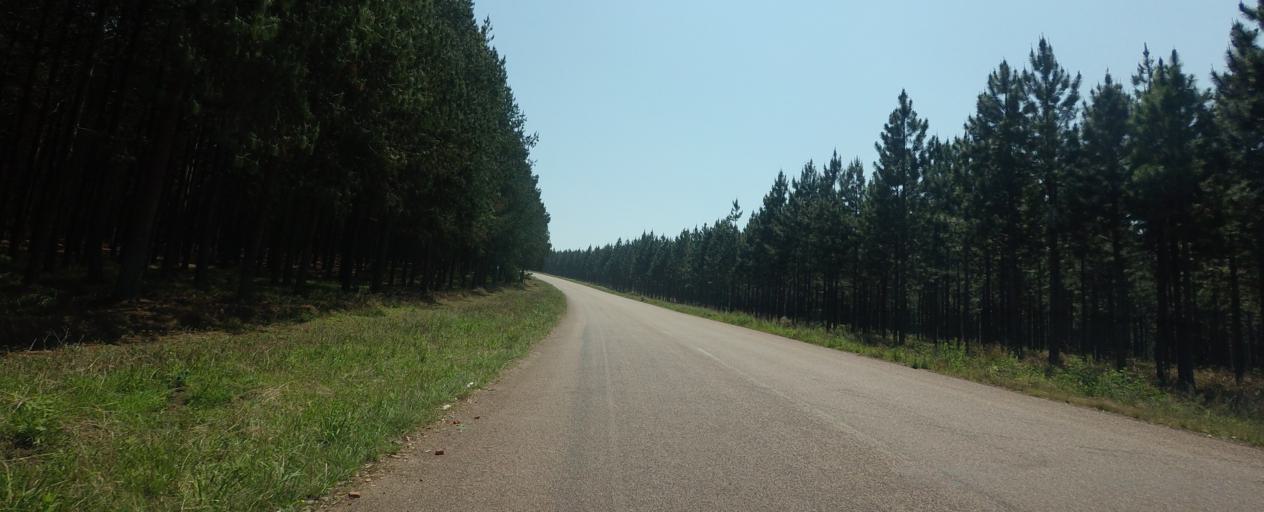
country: ZA
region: Mpumalanga
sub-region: Ehlanzeni District
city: Graksop
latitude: -25.0528
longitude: 30.8187
